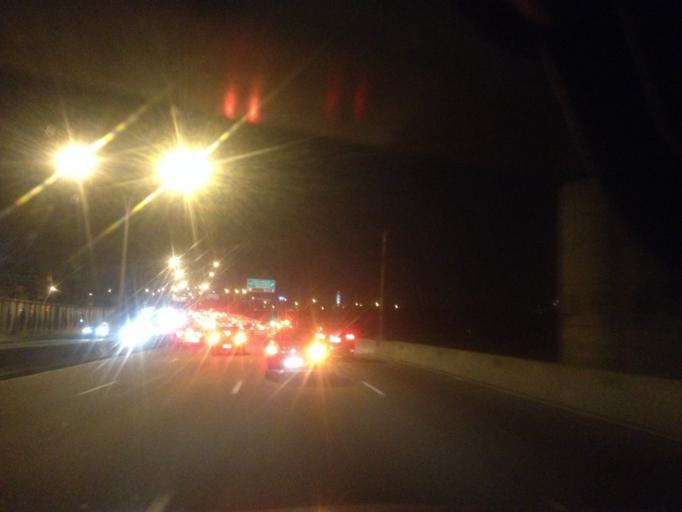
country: BR
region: Rio de Janeiro
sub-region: Rio De Janeiro
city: Rio de Janeiro
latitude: -22.8671
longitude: -43.2328
